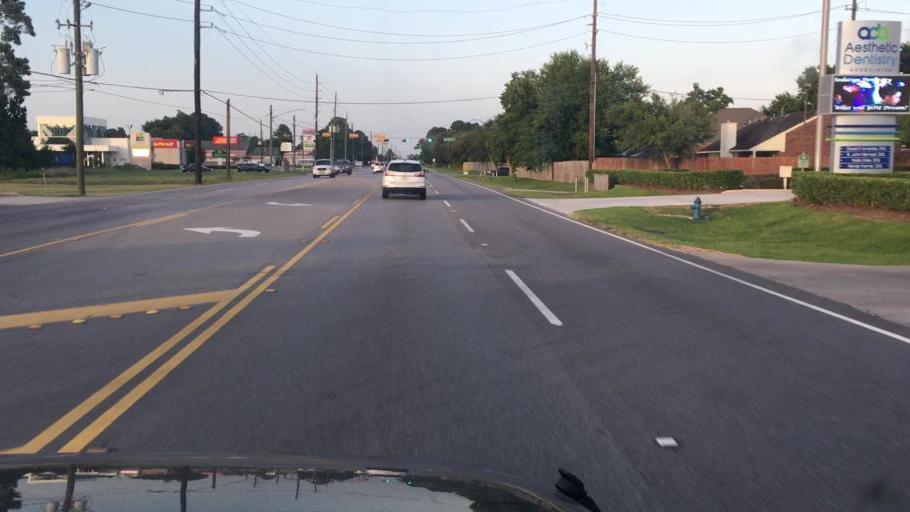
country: US
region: Texas
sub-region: Harris County
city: Atascocita
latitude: 29.9942
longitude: -95.1753
